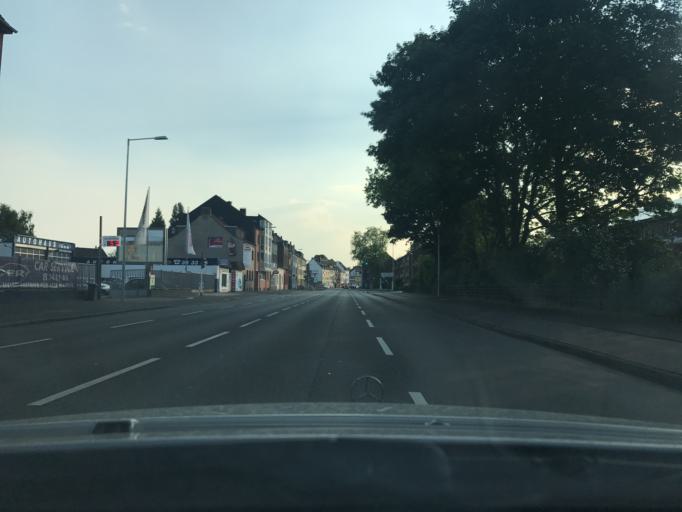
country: DE
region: North Rhine-Westphalia
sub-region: Regierungsbezirk Dusseldorf
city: Krefeld
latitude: 51.3350
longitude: 6.5965
